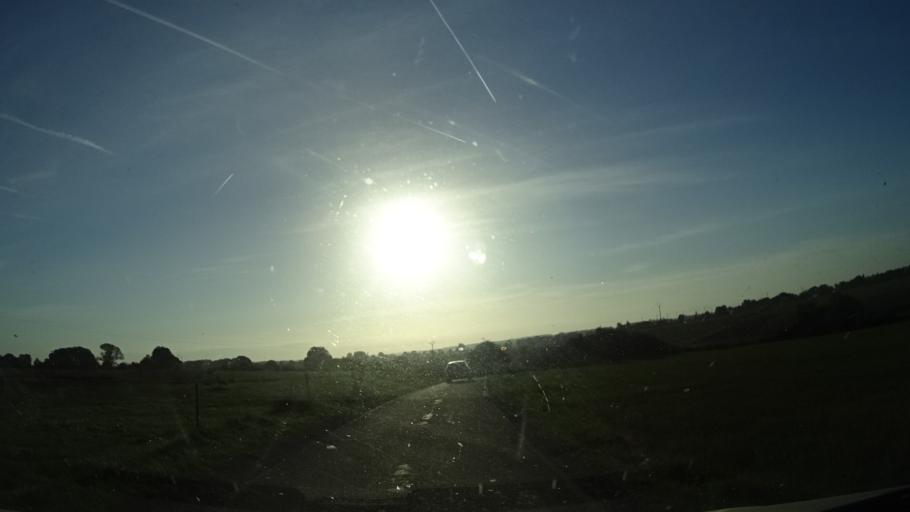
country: BE
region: Wallonia
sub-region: Province du Hainaut
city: Beaumont
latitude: 50.2564
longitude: 4.2494
